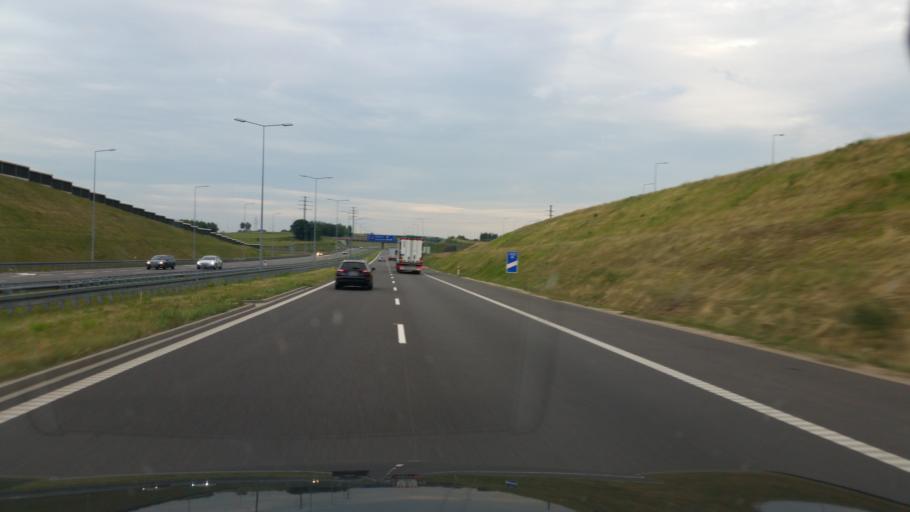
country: PL
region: Silesian Voivodeship
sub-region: Powiat rybnicki
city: Swierklany Gorne
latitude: 50.0310
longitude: 18.6030
